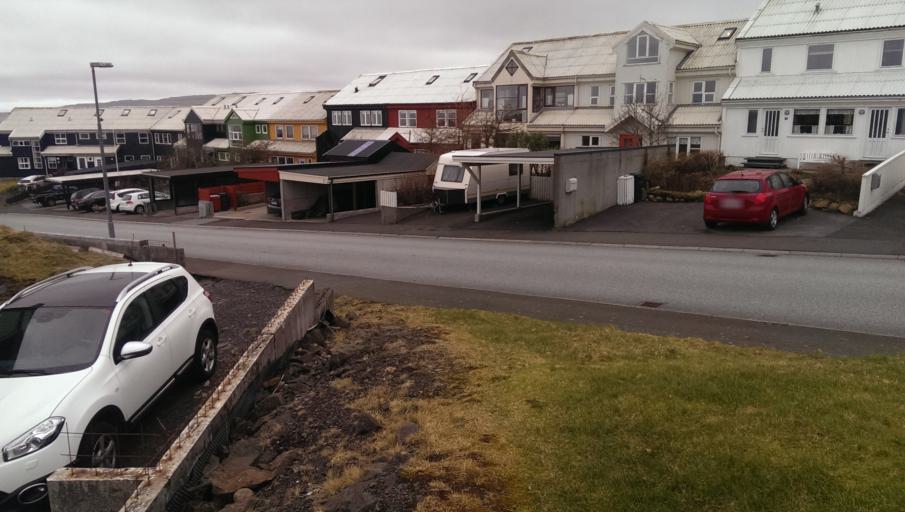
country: FO
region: Streymoy
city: Hoyvik
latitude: 62.0343
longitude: -6.7920
